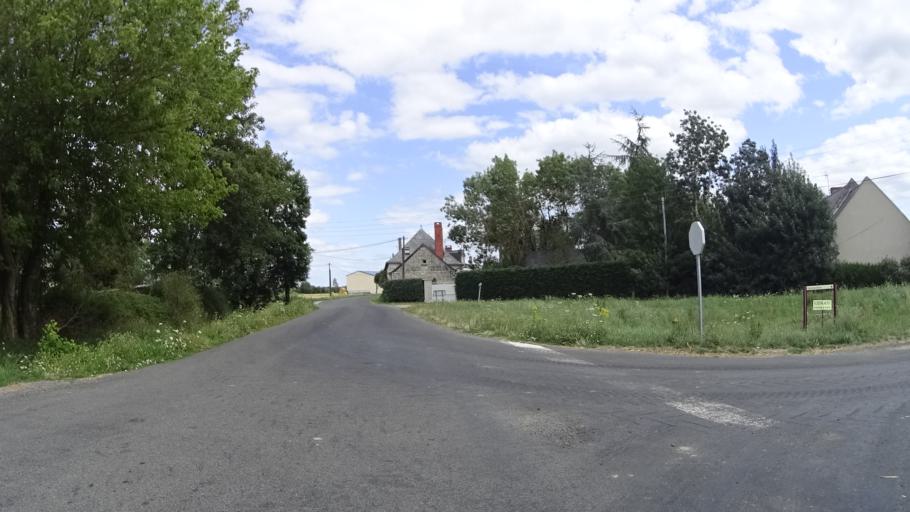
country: FR
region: Pays de la Loire
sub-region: Departement de Maine-et-Loire
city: La Menitre
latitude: 47.4038
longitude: -0.2534
